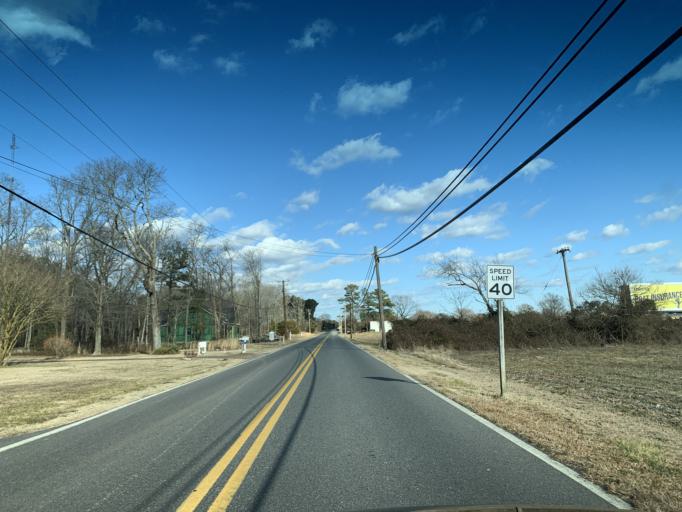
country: US
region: Maryland
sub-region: Worcester County
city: Berlin
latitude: 38.3448
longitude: -75.1878
